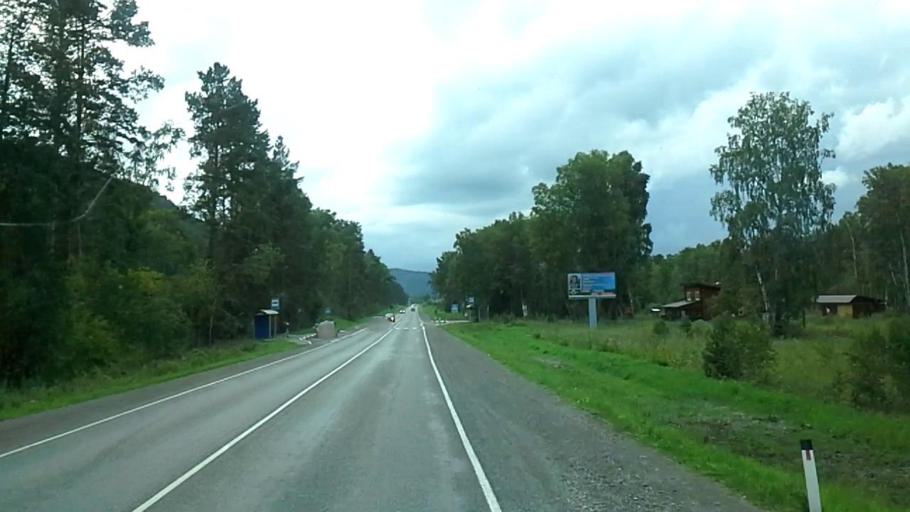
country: RU
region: Altay
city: Souzga
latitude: 51.8742
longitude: 85.8022
